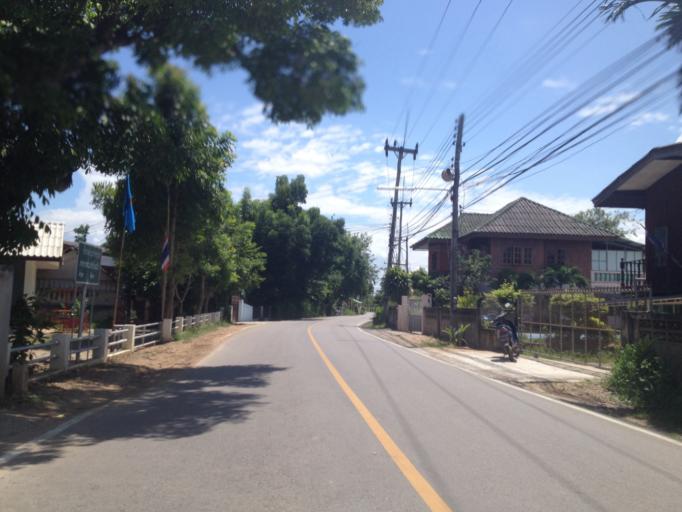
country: TH
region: Chiang Mai
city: Hang Dong
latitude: 18.6846
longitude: 98.9272
